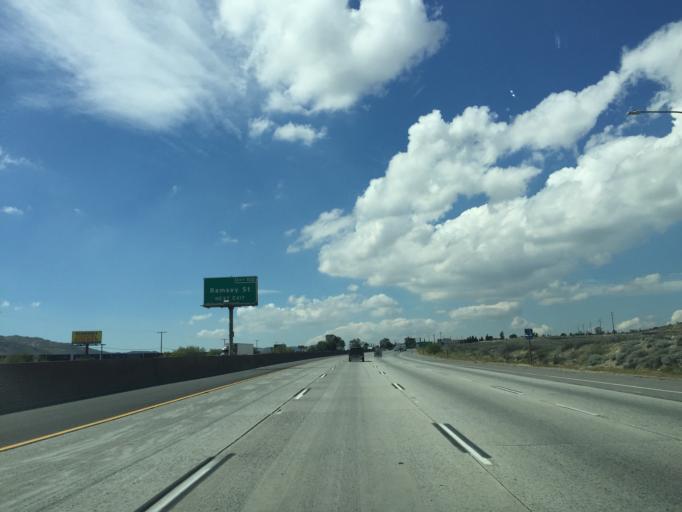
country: US
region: California
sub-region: Riverside County
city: Banning
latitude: 33.9283
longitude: -116.8452
